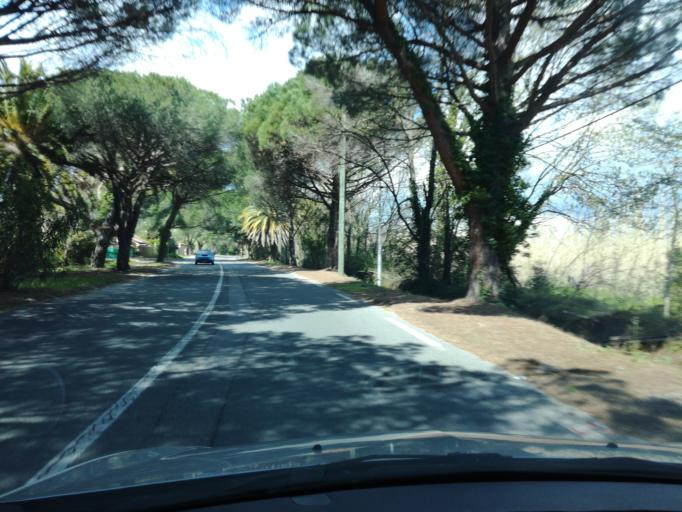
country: FR
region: Provence-Alpes-Cote d'Azur
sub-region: Departement du Var
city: Hyeres
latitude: 43.1078
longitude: 6.1739
